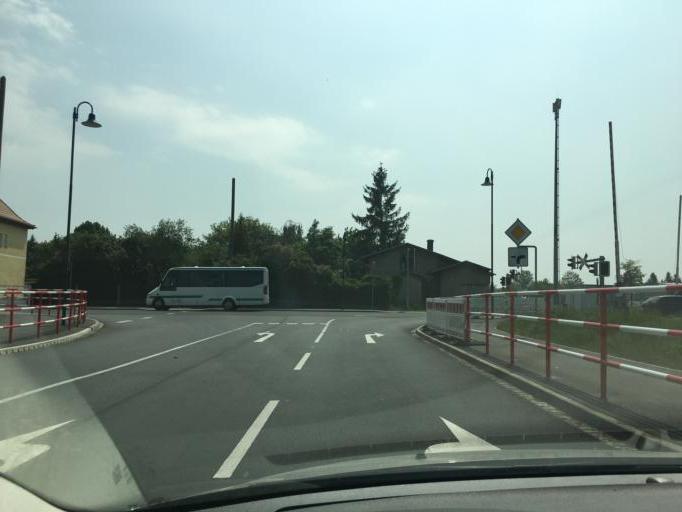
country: DE
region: Saxony
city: Naunhof
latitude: 51.2811
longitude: 12.5926
